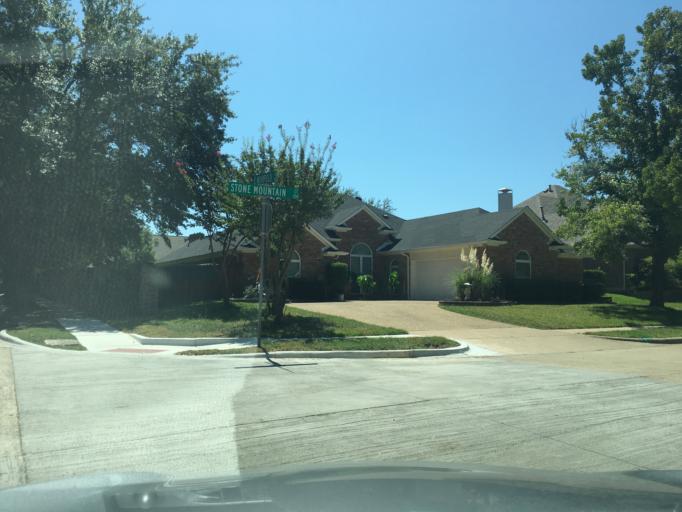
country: US
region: Texas
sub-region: Dallas County
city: Sachse
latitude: 32.9678
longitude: -96.6304
